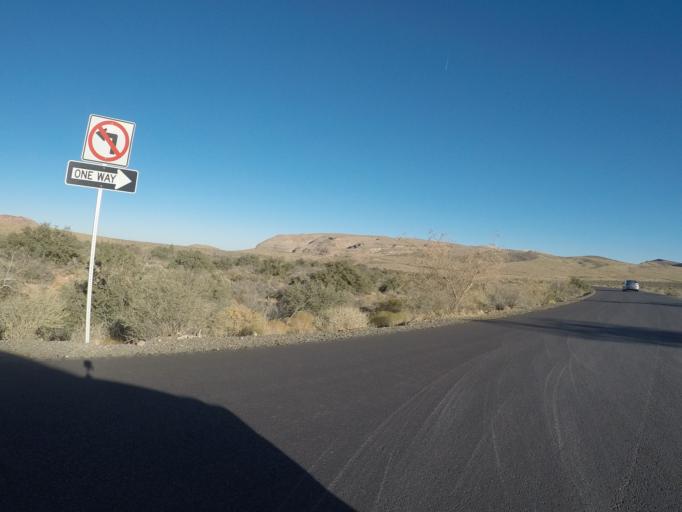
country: US
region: Nevada
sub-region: Clark County
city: Summerlin South
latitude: 36.1171
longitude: -115.4566
